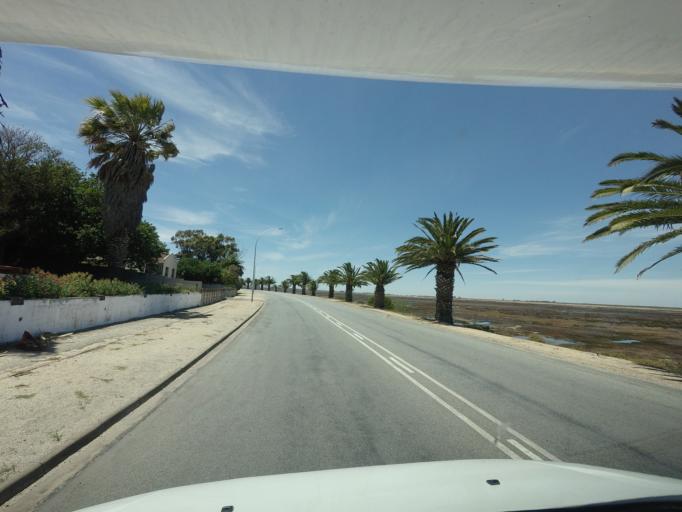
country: ZA
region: Western Cape
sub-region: West Coast District Municipality
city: Vredenburg
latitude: -32.7879
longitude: 18.1781
